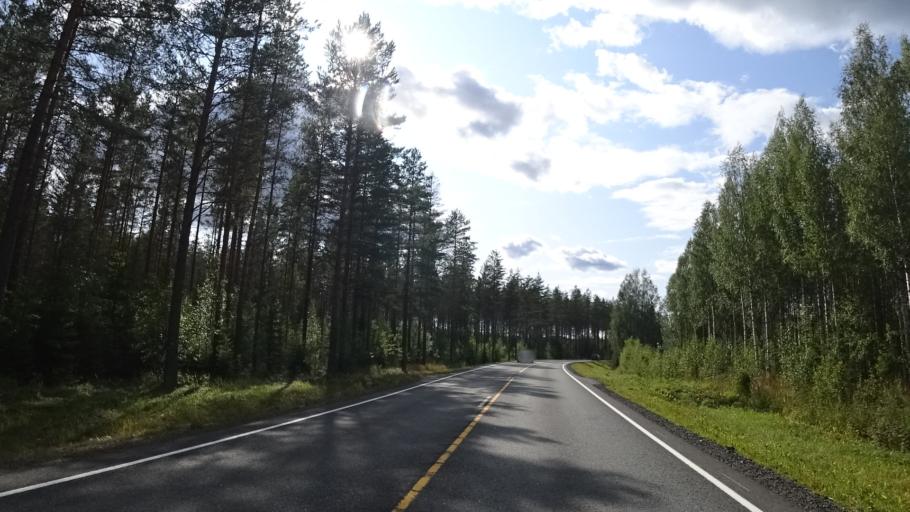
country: FI
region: North Karelia
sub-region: Keski-Karjala
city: Tohmajaervi
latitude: 62.1846
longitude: 30.4837
